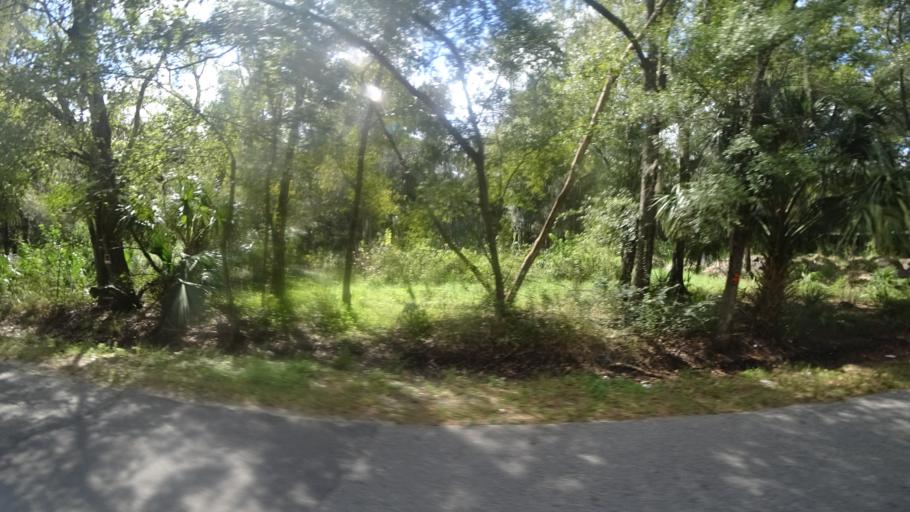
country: US
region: Florida
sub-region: Hillsborough County
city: Sun City Center
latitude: 27.6582
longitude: -82.3643
